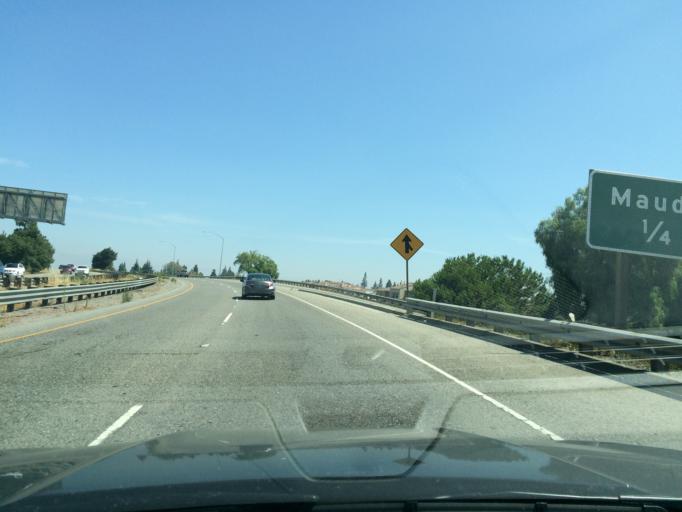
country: US
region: California
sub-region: Santa Clara County
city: Mountain View
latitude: 37.3860
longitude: -122.0606
